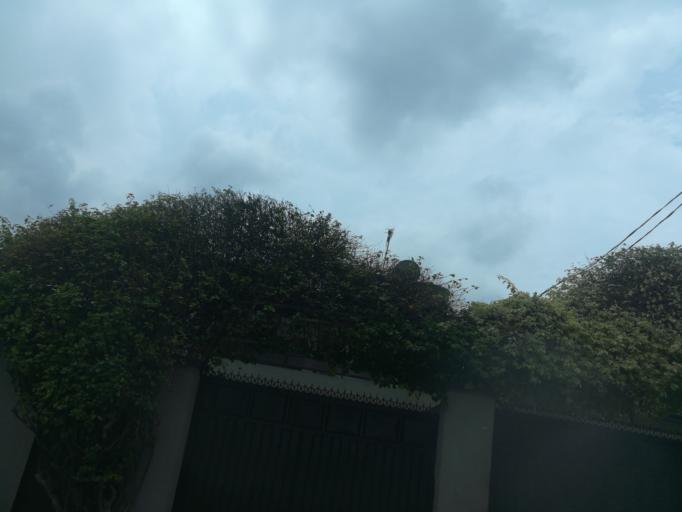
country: NG
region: Lagos
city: Ojota
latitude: 6.5885
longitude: 3.3665
